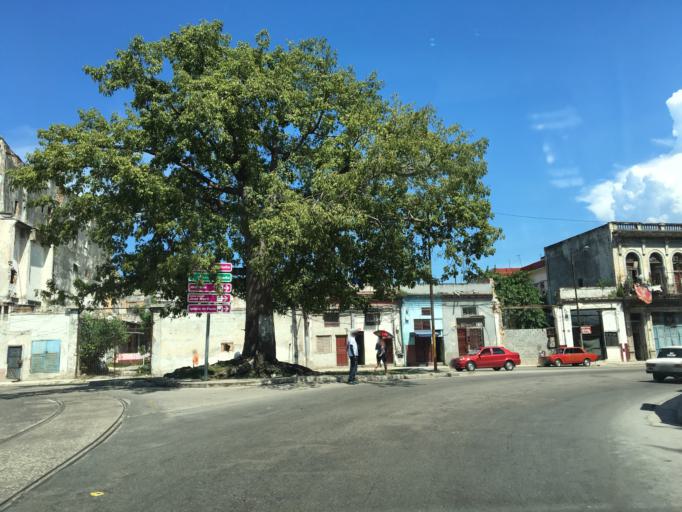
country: CU
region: La Habana
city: La Habana Vieja
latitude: 23.1304
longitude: -82.3547
